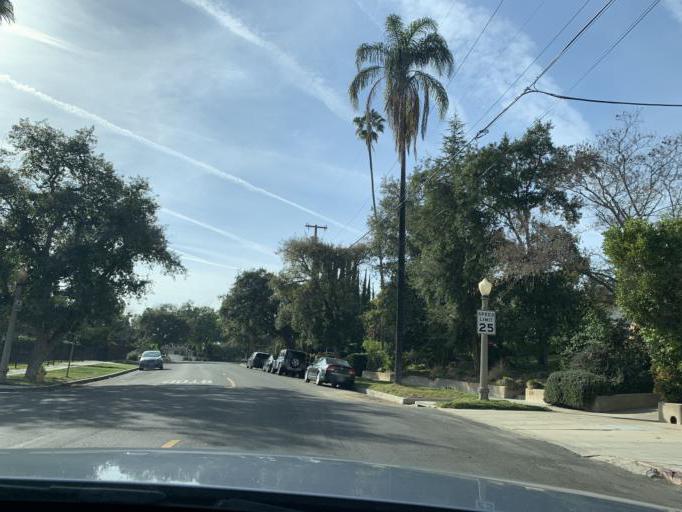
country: US
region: California
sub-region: Los Angeles County
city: Glendale
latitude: 34.1429
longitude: -118.2138
